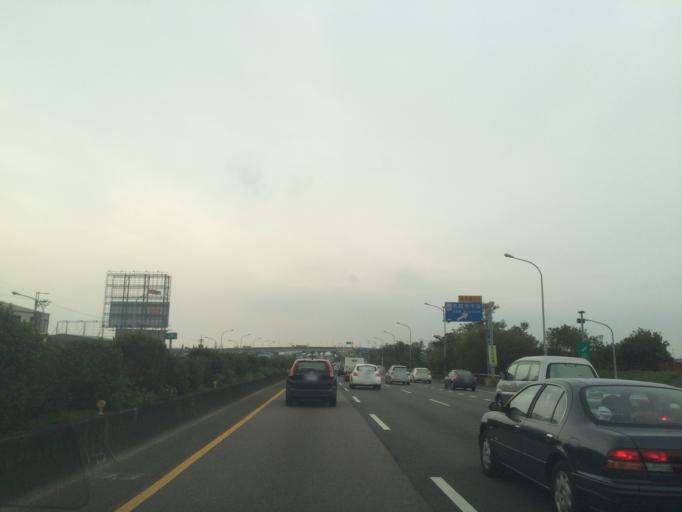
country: TW
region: Taiwan
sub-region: Taichung City
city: Taichung
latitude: 24.1255
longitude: 120.6198
